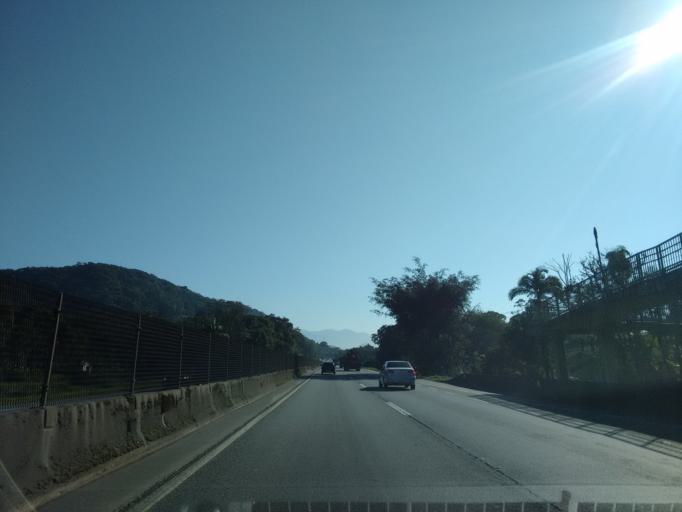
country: BR
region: Santa Catarina
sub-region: Joinville
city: Joinville
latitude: -26.2181
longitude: -48.9160
